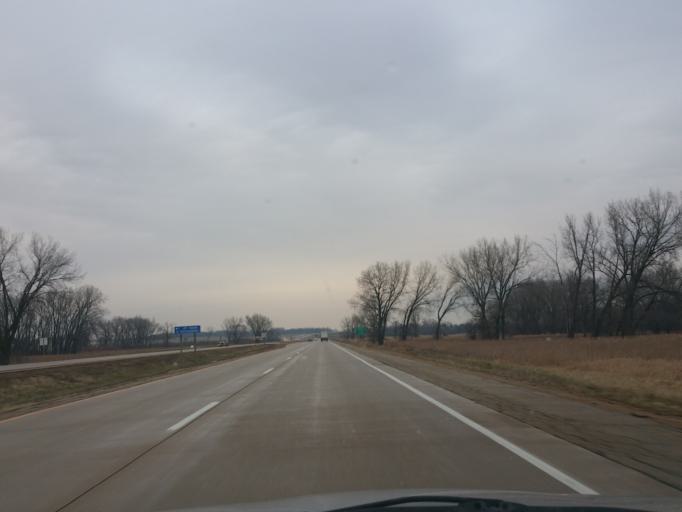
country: US
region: Wisconsin
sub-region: Dane County
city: Maple Bluff
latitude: 43.1378
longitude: -89.3224
